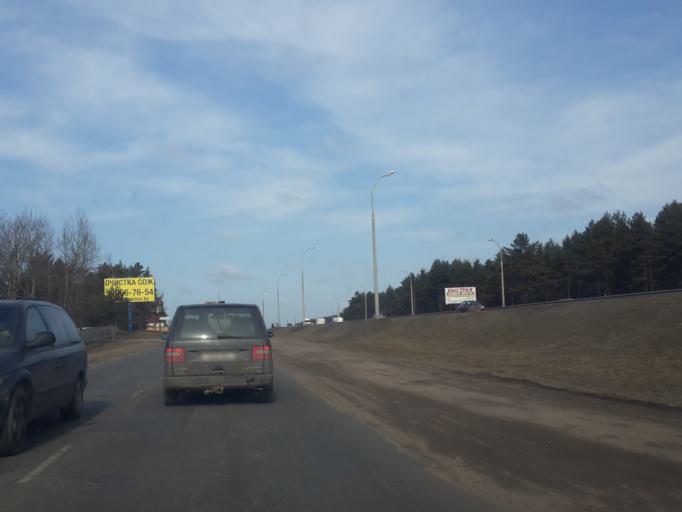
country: BY
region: Minsk
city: Vyaliki Trastsyanets
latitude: 53.9040
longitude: 27.6878
